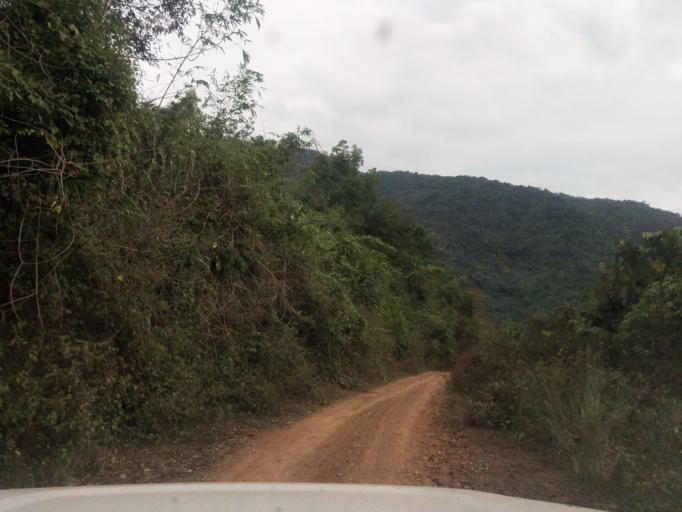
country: LA
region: Phongsali
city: Khoa
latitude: 21.2917
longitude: 102.5836
